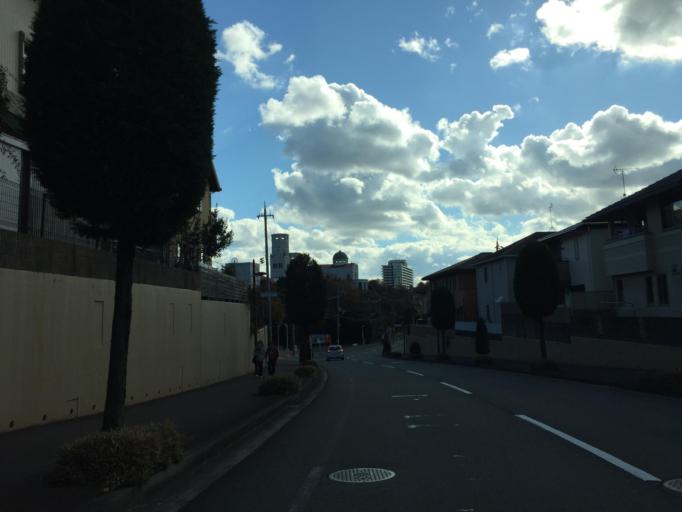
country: JP
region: Wakayama
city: Wakayama-shi
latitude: 34.2696
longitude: 135.1482
